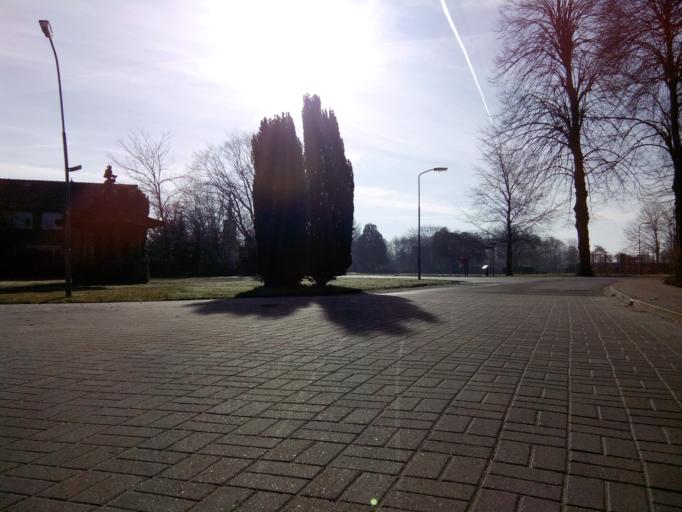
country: NL
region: Gelderland
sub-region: Gemeente Barneveld
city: Terschuur
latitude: 52.1201
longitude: 5.5060
